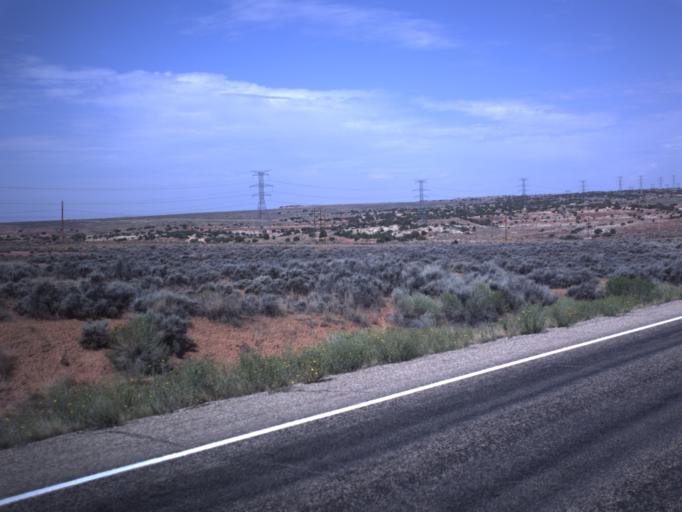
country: US
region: Utah
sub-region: Uintah County
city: Naples
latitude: 40.1602
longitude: -109.3095
